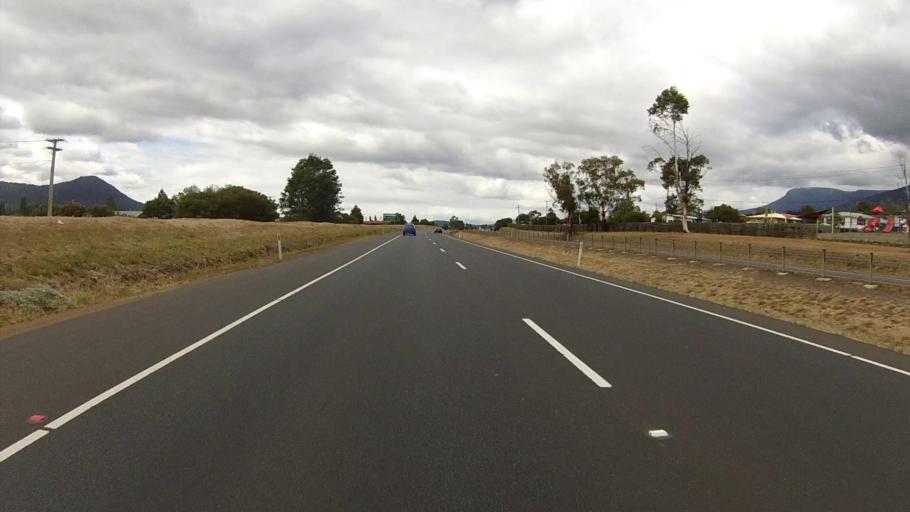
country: AU
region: Tasmania
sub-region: Glenorchy
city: Claremont
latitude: -42.7841
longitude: 147.2409
